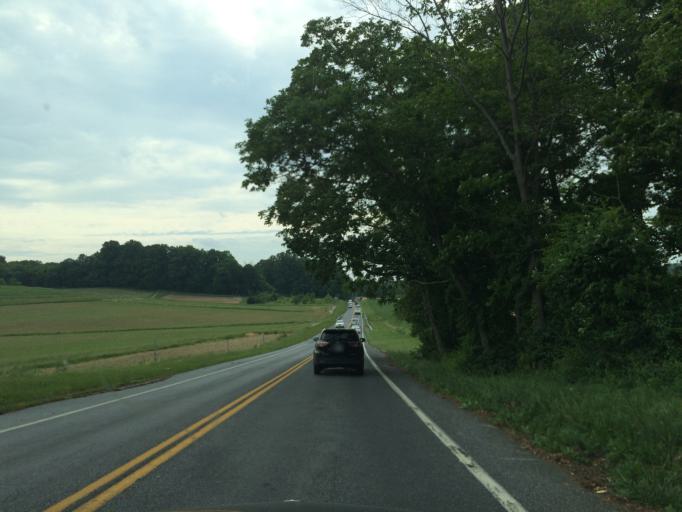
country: US
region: Maryland
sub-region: Howard County
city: Highland
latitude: 39.2477
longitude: -76.9245
